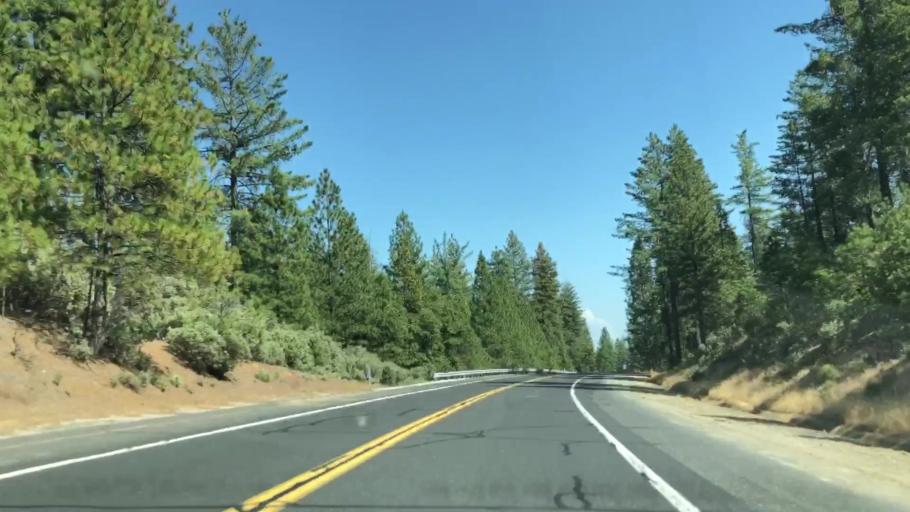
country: US
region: California
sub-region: Tuolumne County
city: Tuolumne City
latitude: 37.8275
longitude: -120.1793
